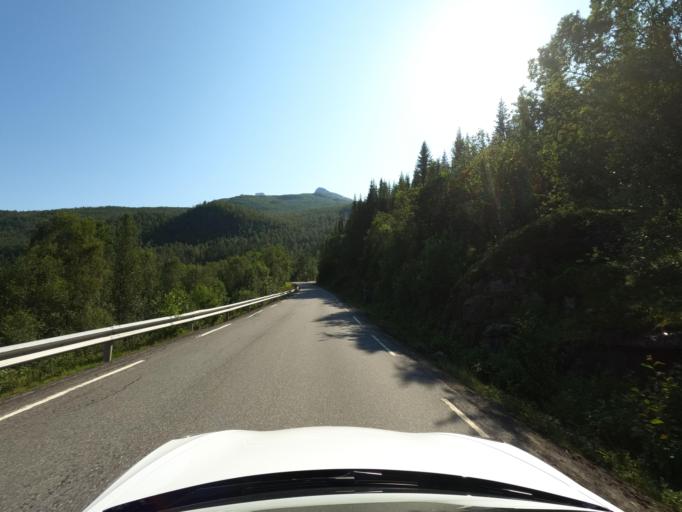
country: NO
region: Nordland
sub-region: Narvik
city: Narvik
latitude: 68.3842
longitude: 17.3470
